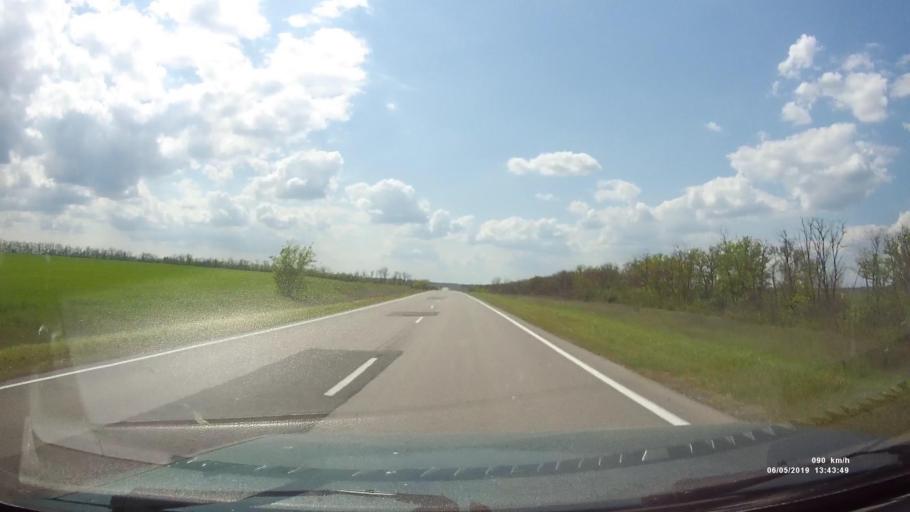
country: RU
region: Rostov
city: Semikarakorsk
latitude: 47.6606
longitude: 40.6310
